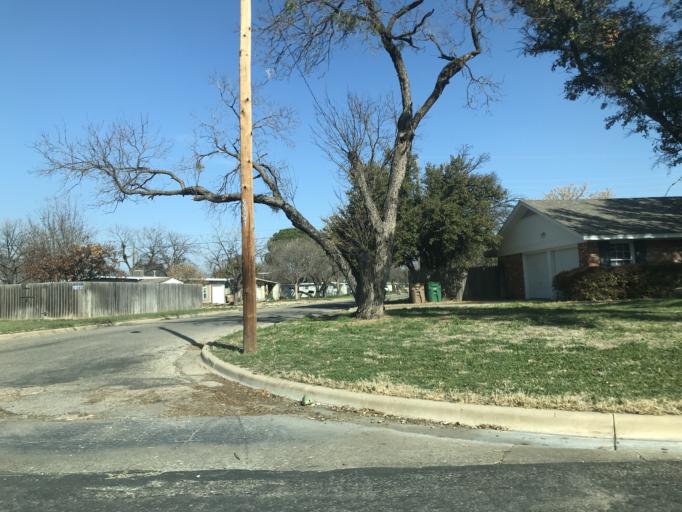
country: US
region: Texas
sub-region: Tom Green County
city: San Angelo
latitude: 31.4351
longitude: -100.4713
